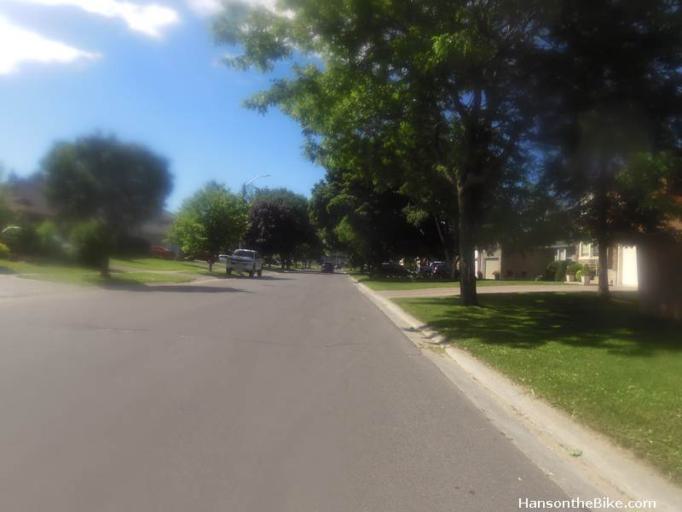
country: CA
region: Ontario
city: Kingston
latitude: 44.2275
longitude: -76.5317
